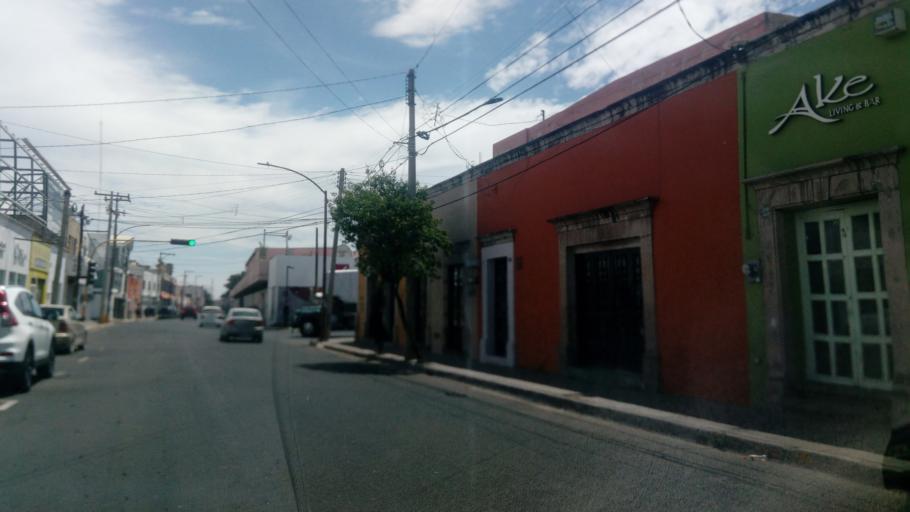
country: MX
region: Durango
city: Victoria de Durango
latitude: 24.0270
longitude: -104.6648
